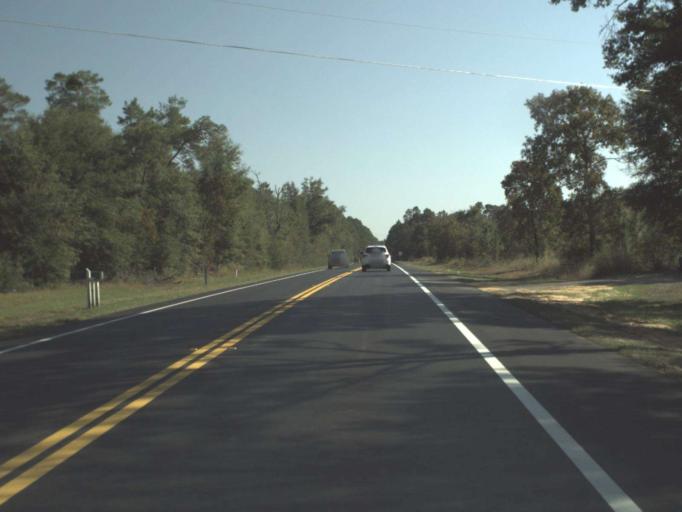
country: US
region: Florida
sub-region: Walton County
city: DeFuniak Springs
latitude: 30.7651
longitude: -86.1540
